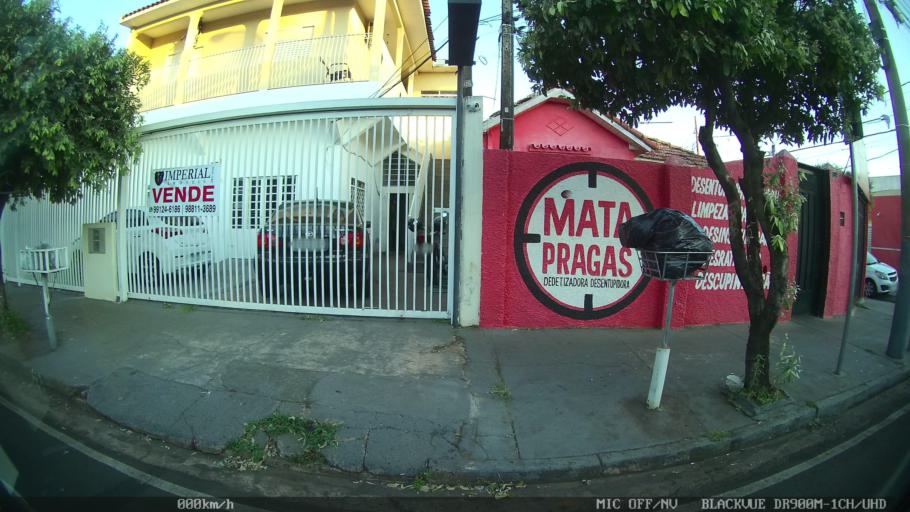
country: BR
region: Sao Paulo
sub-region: Sao Jose Do Rio Preto
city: Sao Jose do Rio Preto
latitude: -20.8042
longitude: -49.3643
